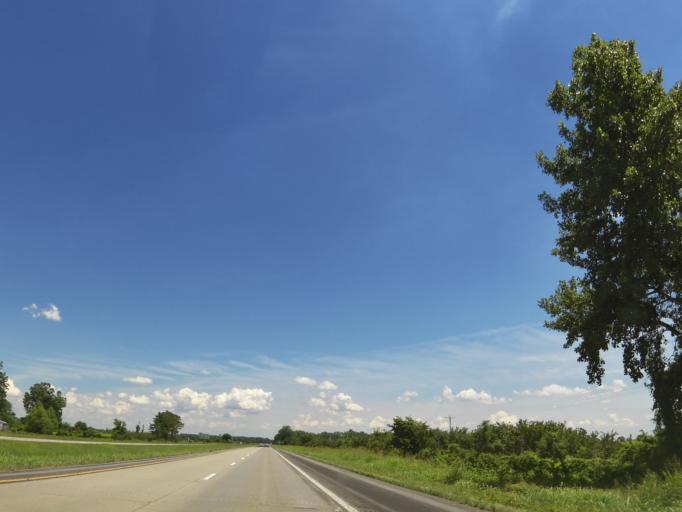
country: US
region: Missouri
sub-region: Pemiscot County
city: Caruthersville
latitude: 36.1470
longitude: -89.6536
